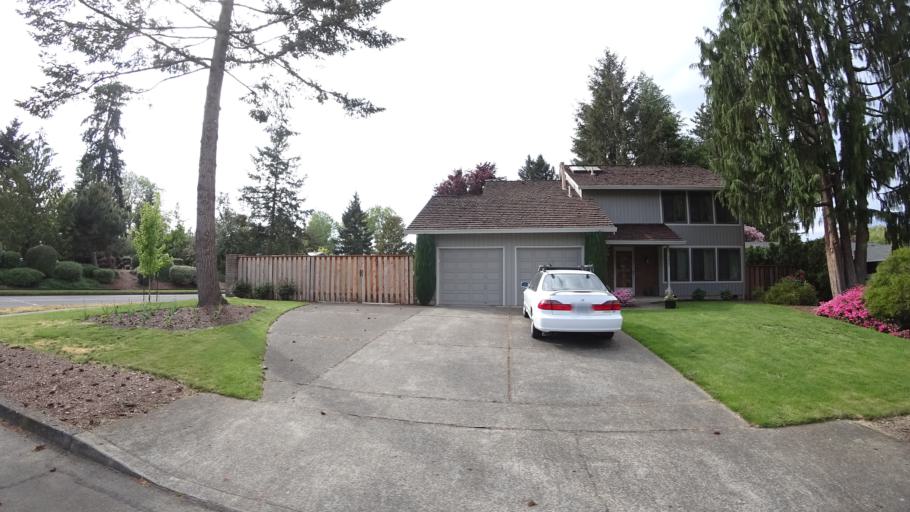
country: US
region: Oregon
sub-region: Washington County
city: Hillsboro
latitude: 45.4985
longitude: -122.9589
